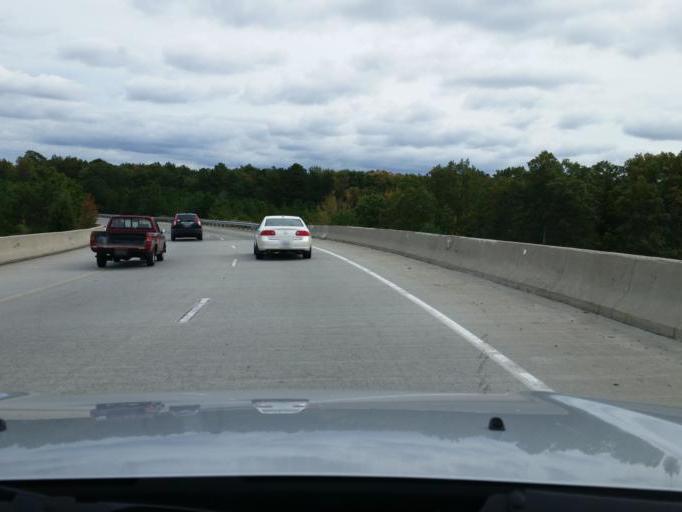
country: US
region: Virginia
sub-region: Henrico County
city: Sandston
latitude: 37.5185
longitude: -77.2703
